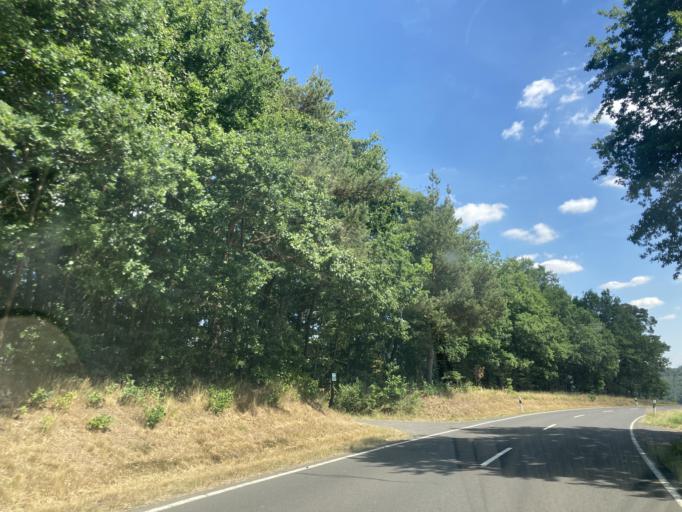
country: DE
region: Hesse
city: Grebenau
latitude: 50.7211
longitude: 9.4359
